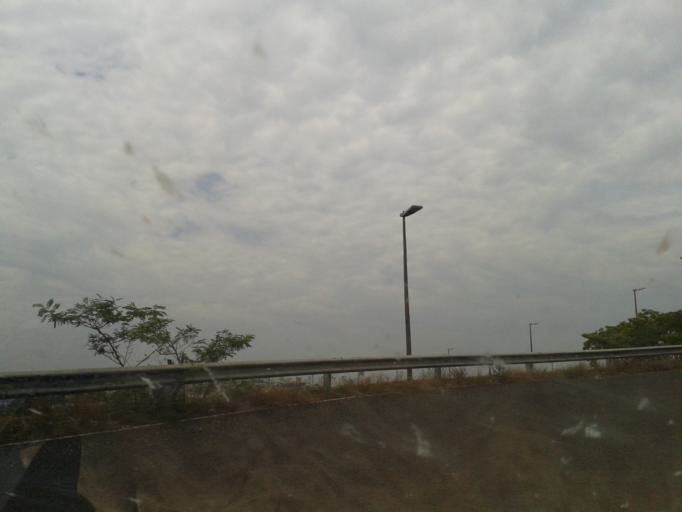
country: BR
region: Minas Gerais
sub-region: Uberlandia
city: Uberlandia
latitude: -18.9079
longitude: -48.3123
